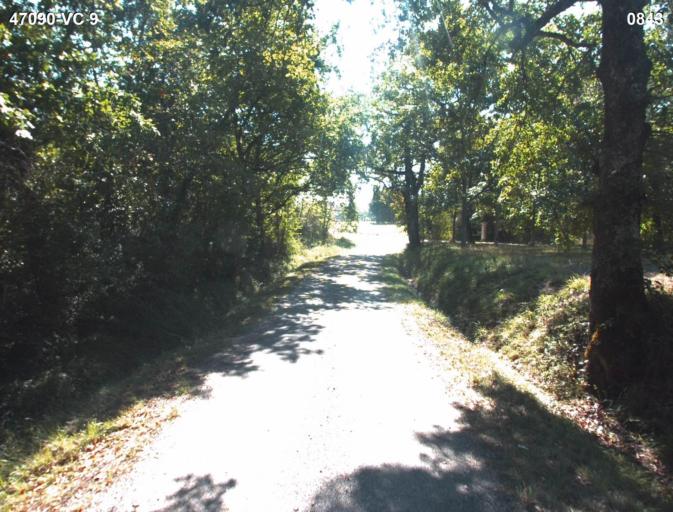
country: FR
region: Aquitaine
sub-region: Departement du Lot-et-Garonne
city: Nerac
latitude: 44.1797
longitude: 0.3874
